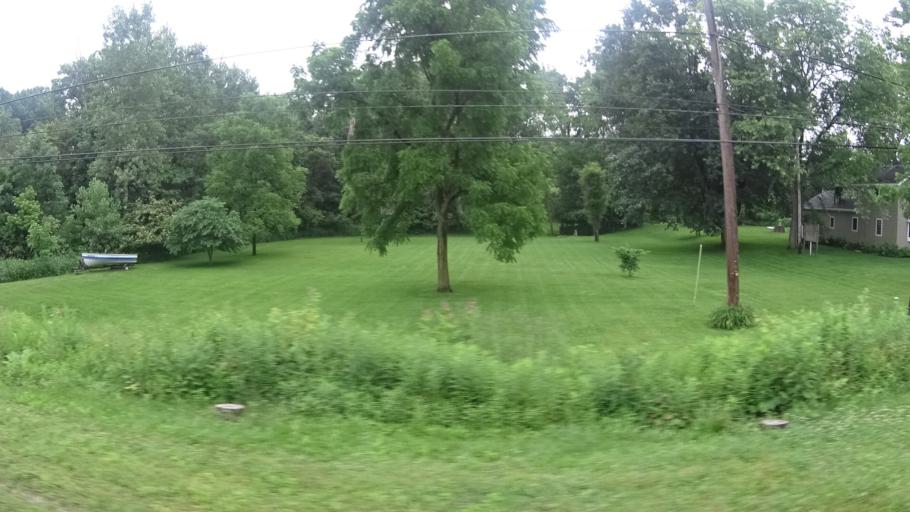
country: US
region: Ohio
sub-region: Erie County
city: Milan
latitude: 41.3031
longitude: -82.6079
